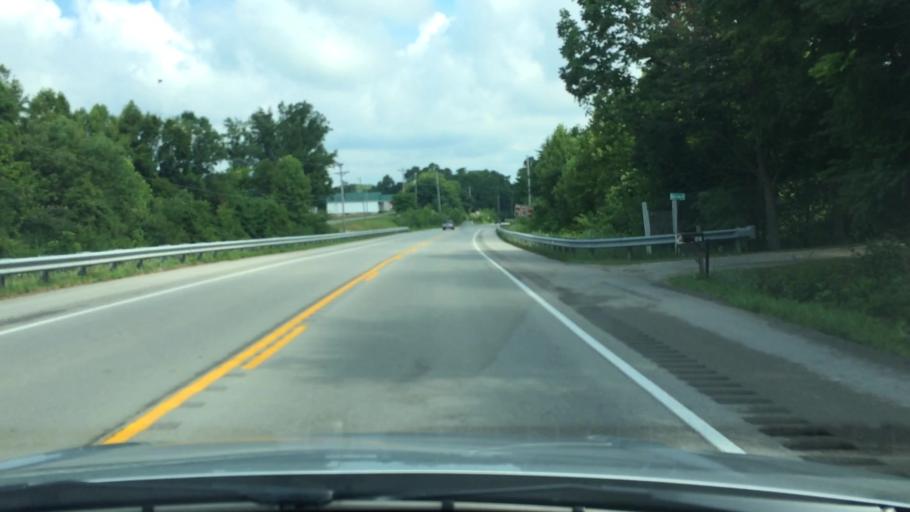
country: US
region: Kentucky
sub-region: McCreary County
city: Whitley City
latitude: 36.8730
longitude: -84.4935
